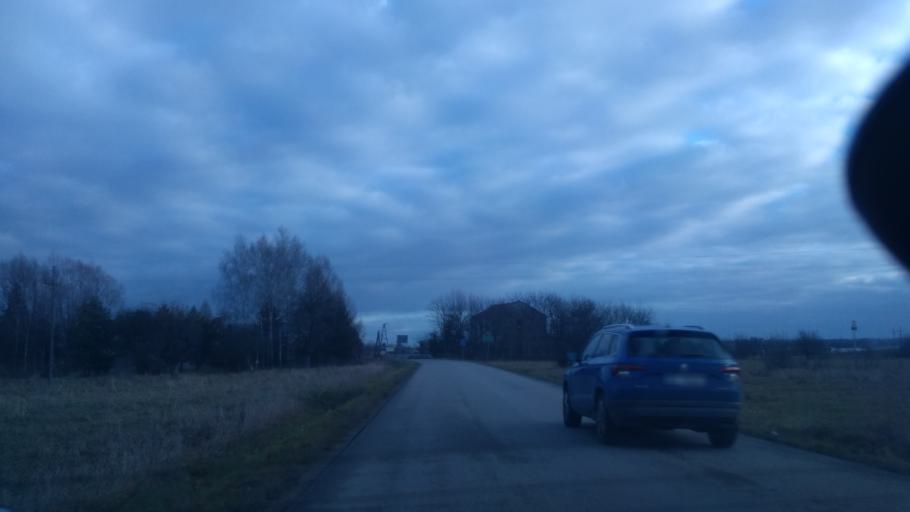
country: PL
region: Subcarpathian Voivodeship
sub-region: Powiat lancucki
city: Czarna
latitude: 50.0943
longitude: 22.1665
